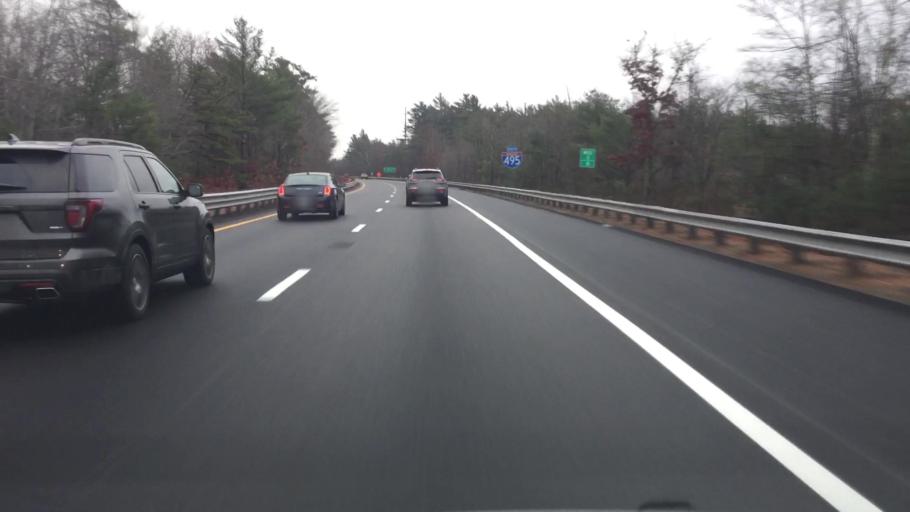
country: US
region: Massachusetts
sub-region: Plymouth County
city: West Wareham
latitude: 41.8132
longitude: -70.7930
